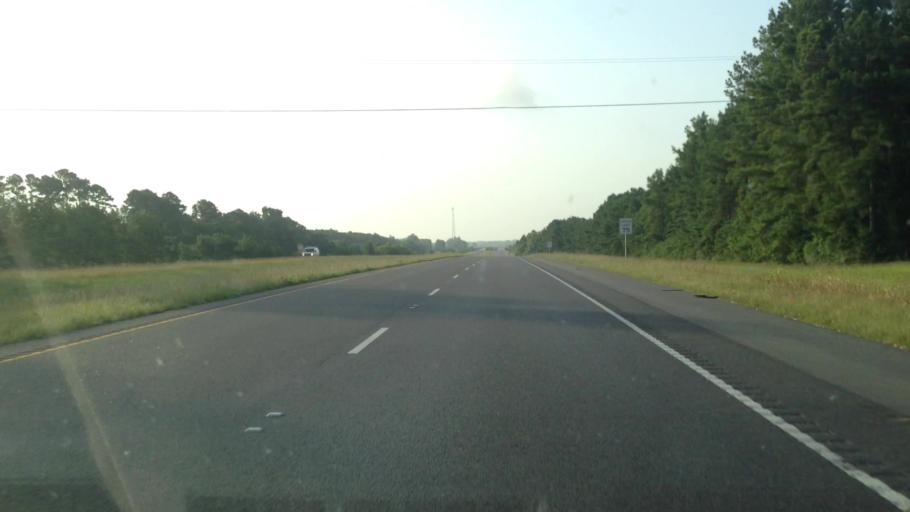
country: US
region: Louisiana
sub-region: Rapides Parish
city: Boyce
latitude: 31.4026
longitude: -92.7074
